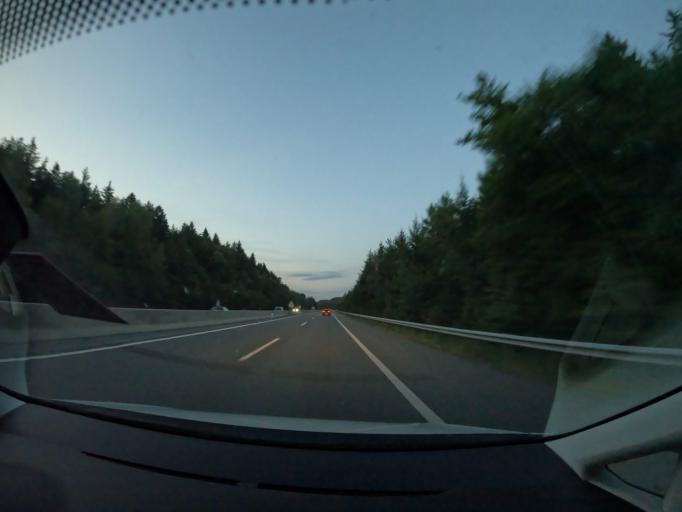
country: AT
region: Styria
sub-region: Politischer Bezirk Hartberg-Fuerstenfeld
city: Bad Waltersdorf
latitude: 47.1456
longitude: 15.9937
